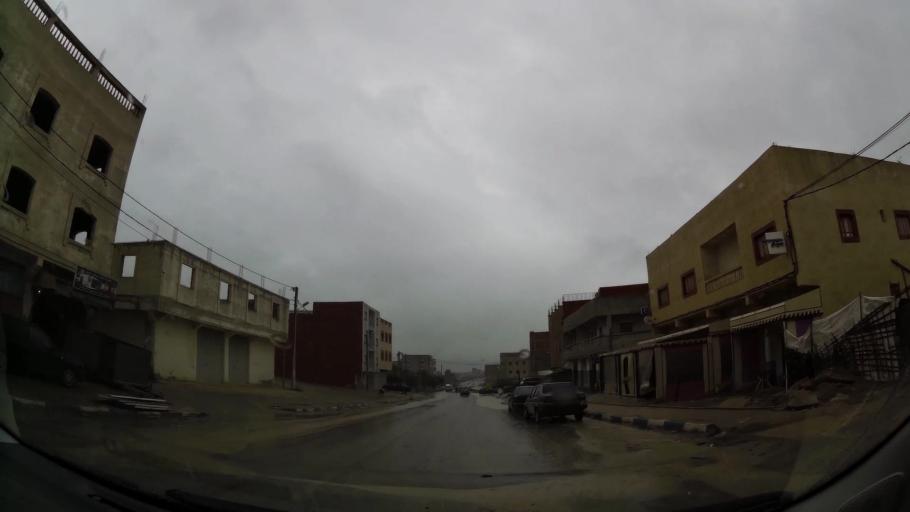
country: MA
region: Oriental
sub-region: Nador
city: Midar
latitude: 34.8831
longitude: -3.7267
